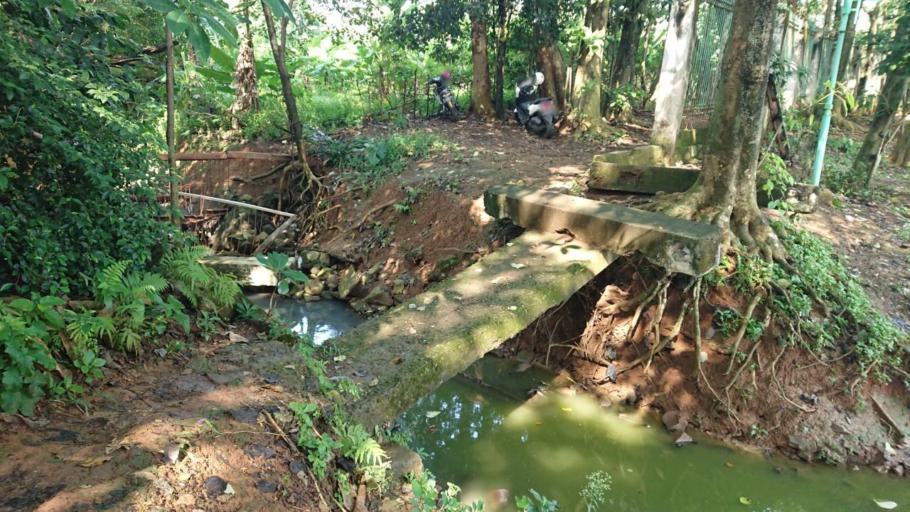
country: ID
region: West Java
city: Depok
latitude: -6.3597
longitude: 106.8869
